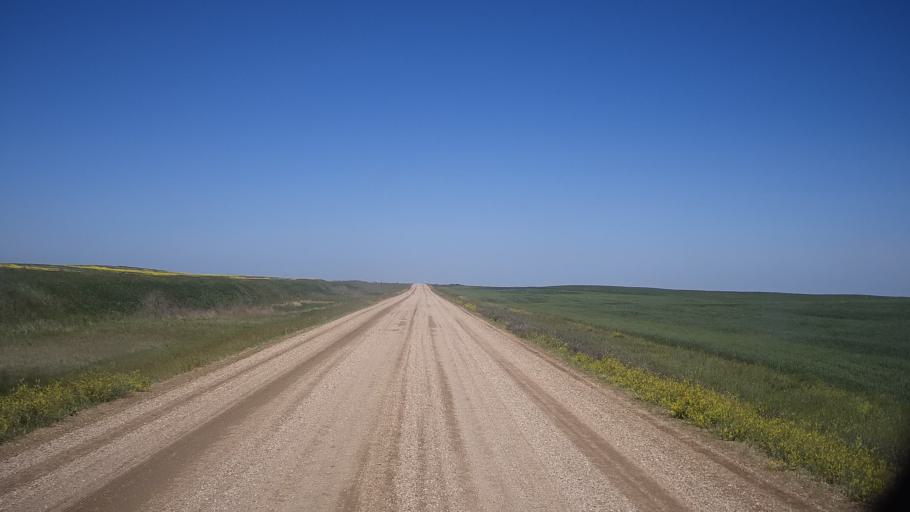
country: CA
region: Saskatchewan
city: Watrous
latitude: 51.8502
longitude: -105.9335
